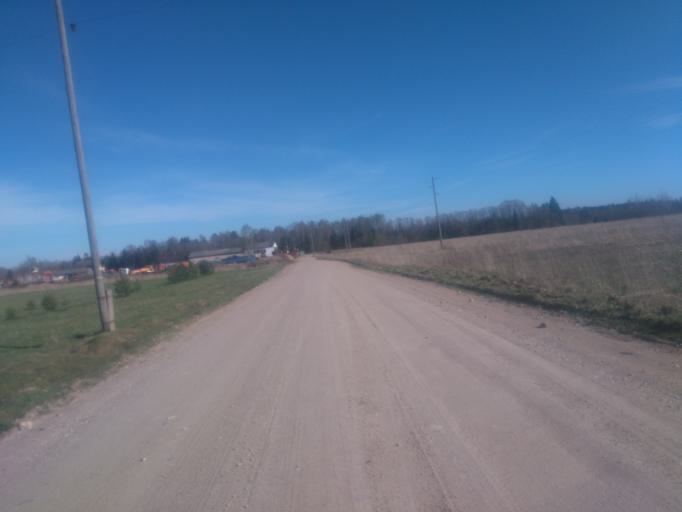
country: LV
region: Vecpiebalga
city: Vecpiebalga
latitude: 57.0213
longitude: 25.8386
